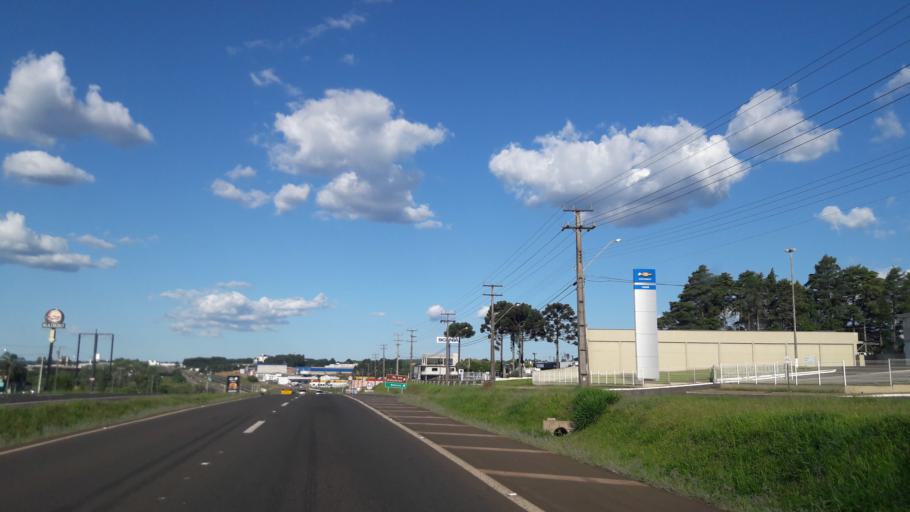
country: BR
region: Parana
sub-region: Guarapuava
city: Guarapuava
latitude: -25.3608
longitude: -51.4688
